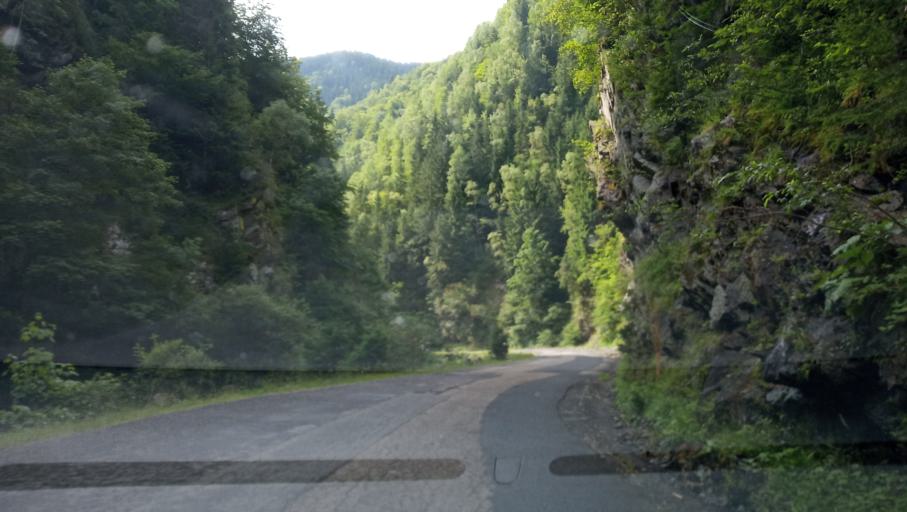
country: RO
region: Hunedoara
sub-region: Oras Petrila
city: Petrila
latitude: 45.4133
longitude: 23.4732
